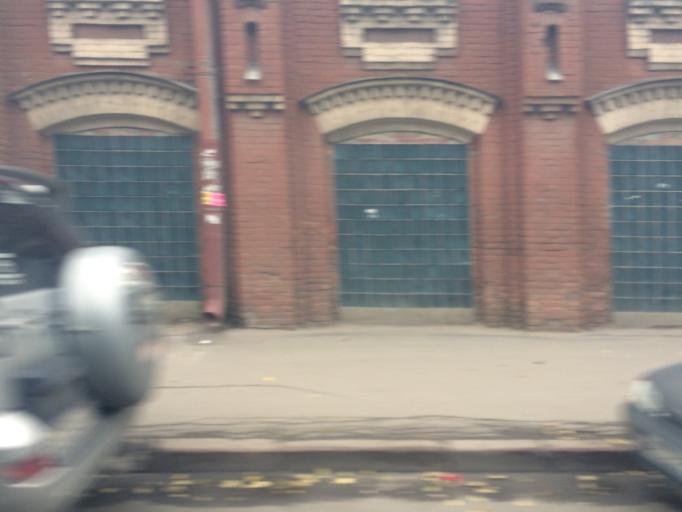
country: RU
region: Leningrad
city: Rybatskoye
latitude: 59.8613
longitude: 30.4779
